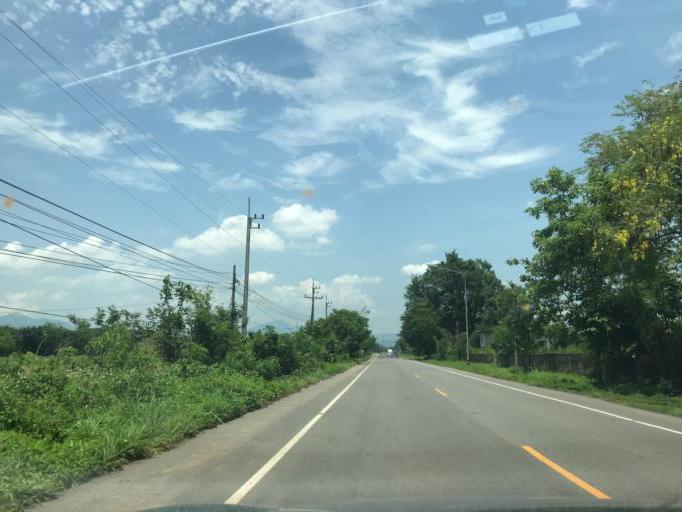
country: TH
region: Phayao
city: Phu Sang
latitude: 19.5837
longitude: 100.3072
